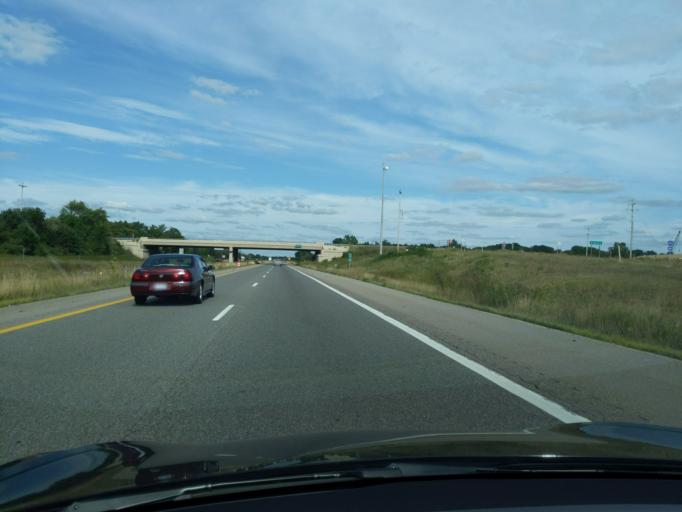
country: US
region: Michigan
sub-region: Muskegon County
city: Fruitport
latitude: 43.0720
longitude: -86.0694
